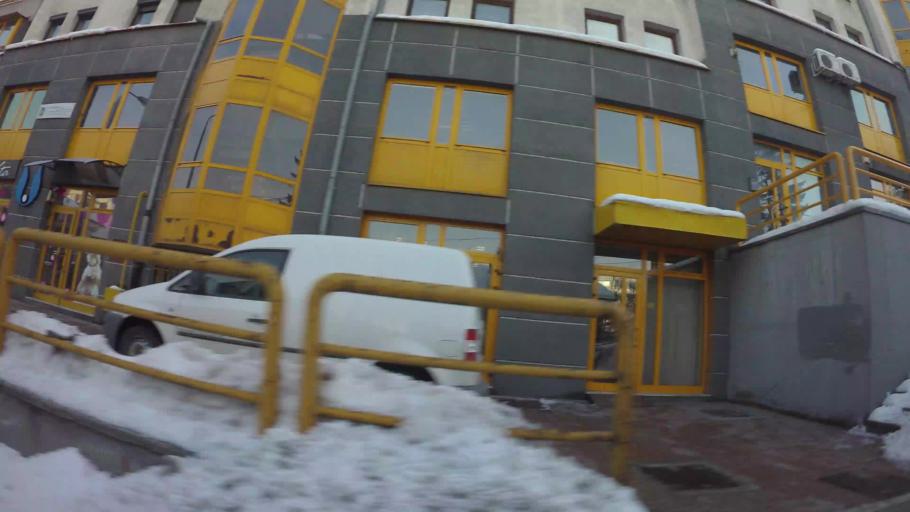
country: BA
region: Federation of Bosnia and Herzegovina
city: Kobilja Glava
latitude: 43.8488
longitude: 18.3972
